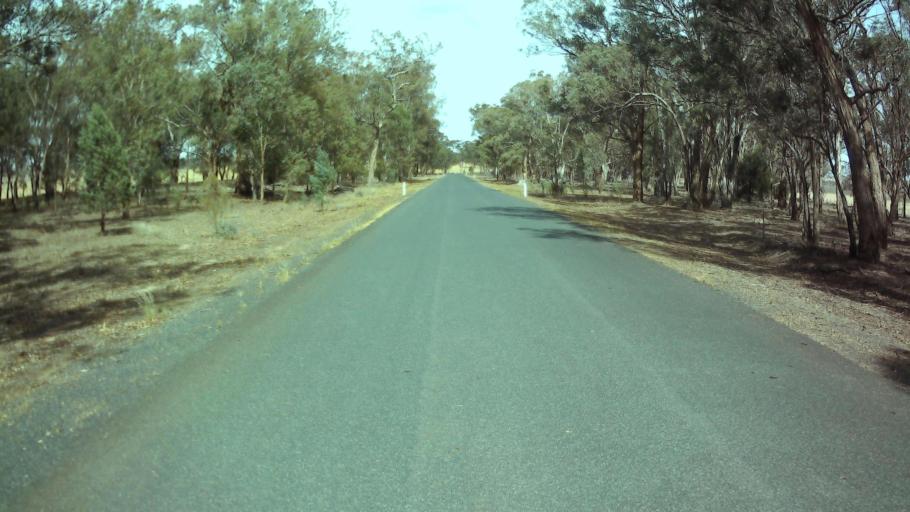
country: AU
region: New South Wales
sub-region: Weddin
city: Grenfell
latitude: -33.8087
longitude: 148.0706
